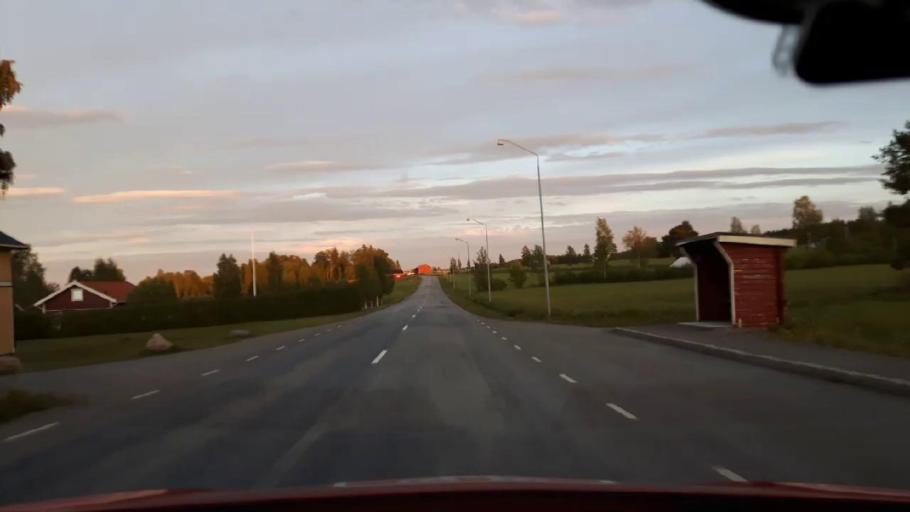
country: SE
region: Jaemtland
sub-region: OEstersunds Kommun
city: Brunflo
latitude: 63.1049
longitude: 14.7366
